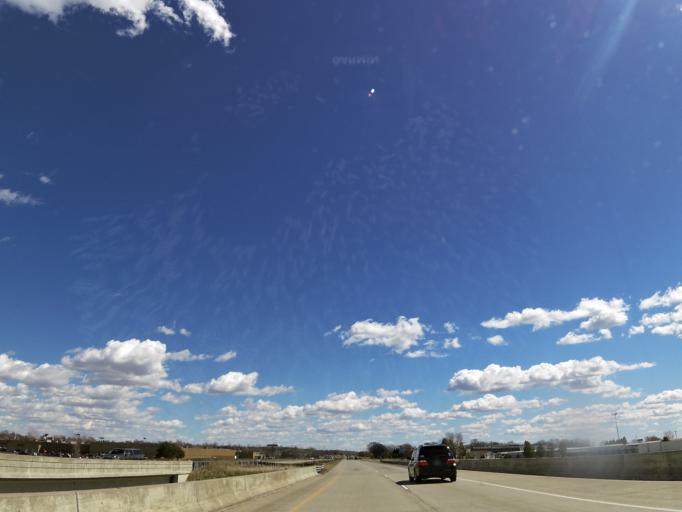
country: US
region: Minnesota
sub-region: Washington County
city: Cottage Grove
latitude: 44.8153
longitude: -92.9348
